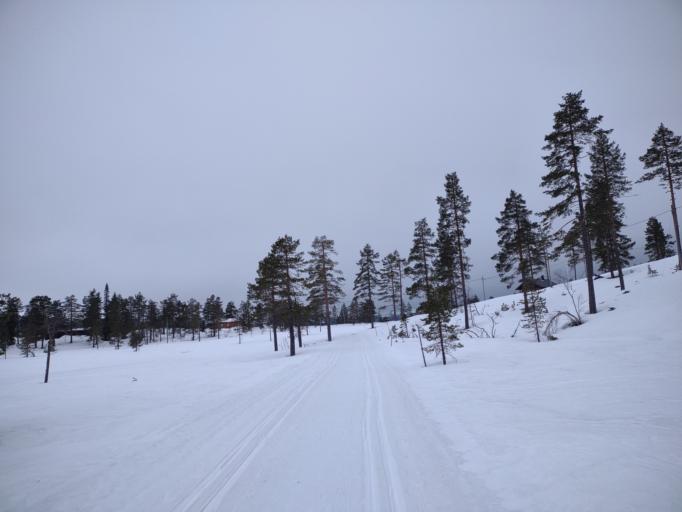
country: NO
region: Buskerud
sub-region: Flesberg
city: Lampeland
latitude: 59.7955
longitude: 9.4365
